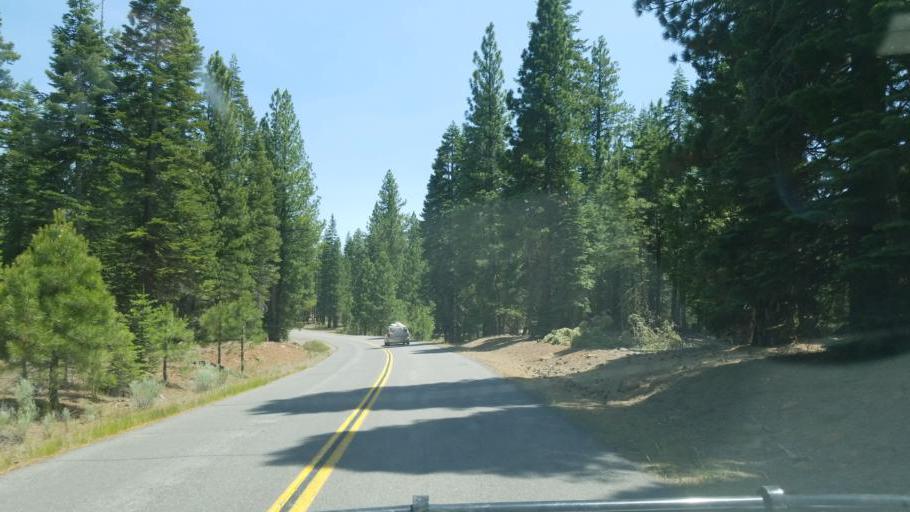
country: US
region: California
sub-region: Lassen County
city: Susanville
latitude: 40.5498
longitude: -120.8162
